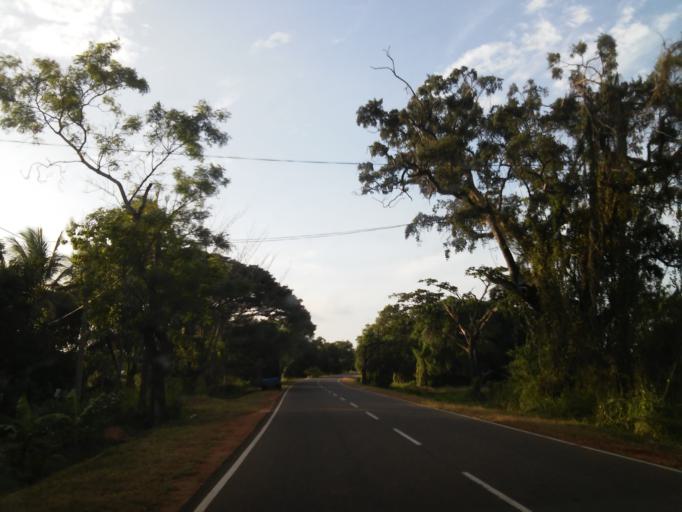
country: LK
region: Central
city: Sigiriya
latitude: 8.1151
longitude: 80.5799
